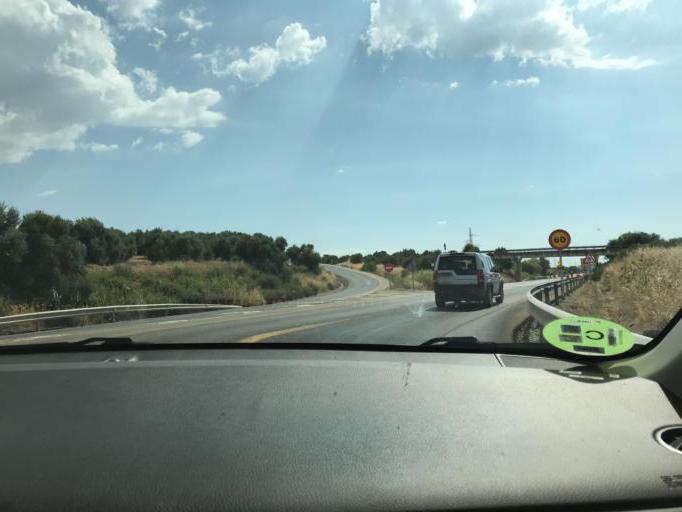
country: ES
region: Andalusia
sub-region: Provincia de Jaen
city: Ubeda
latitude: 38.0259
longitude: -3.3807
